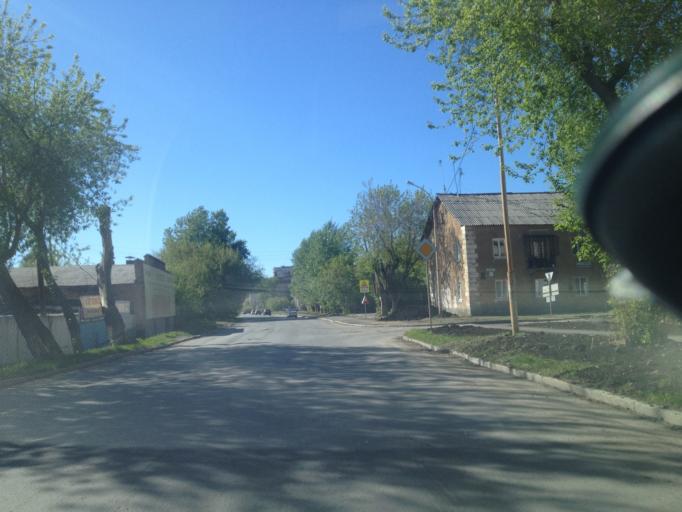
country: RU
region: Sverdlovsk
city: Shuvakish
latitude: 56.8672
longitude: 60.5253
